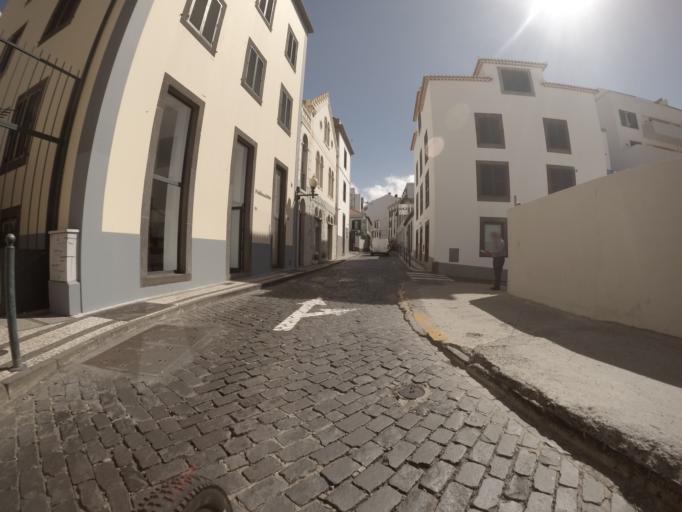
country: PT
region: Madeira
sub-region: Funchal
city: Nossa Senhora do Monte
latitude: 32.6504
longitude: -16.9049
